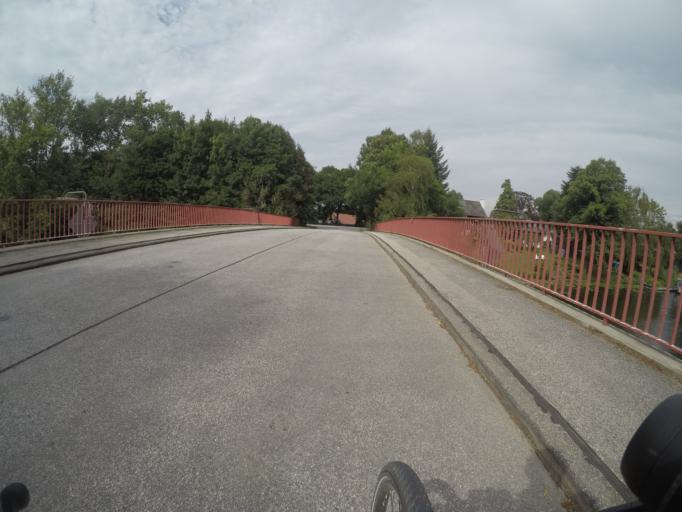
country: DE
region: Schleswig-Holstein
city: Oststeinbek
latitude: 53.4814
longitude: 10.1285
